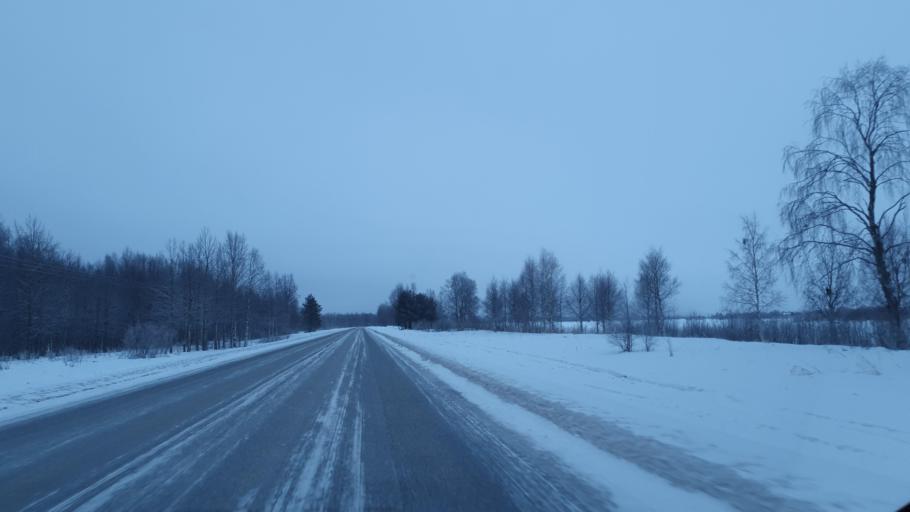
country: SE
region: Norrbotten
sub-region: Overtornea Kommun
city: OEvertornea
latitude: 66.3965
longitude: 23.6835
